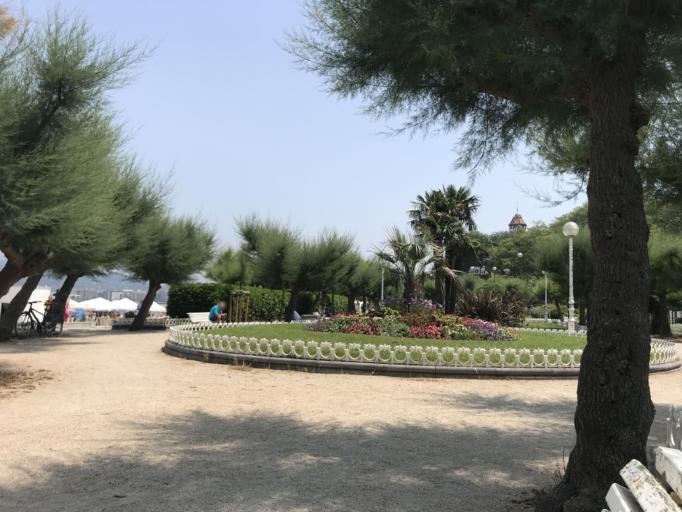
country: ES
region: Basque Country
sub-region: Provincia de Guipuzcoa
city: San Sebastian
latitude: 43.3159
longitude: -2.0016
